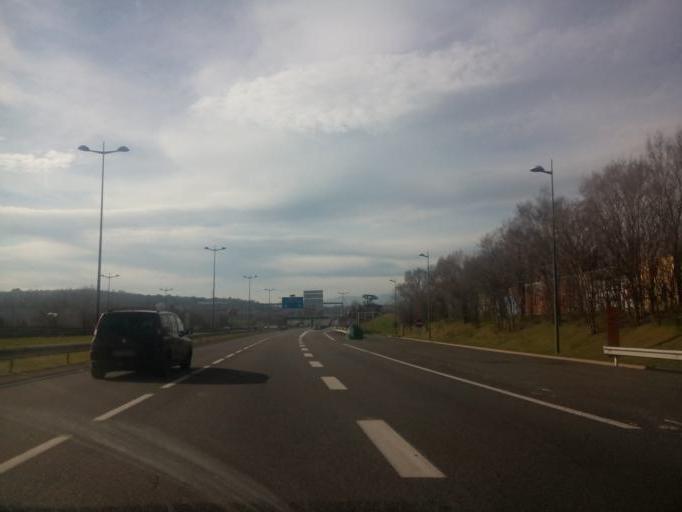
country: FR
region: Rhone-Alpes
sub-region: Departement du Rhone
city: Pierre-Benite
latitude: 45.6962
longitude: 4.8327
